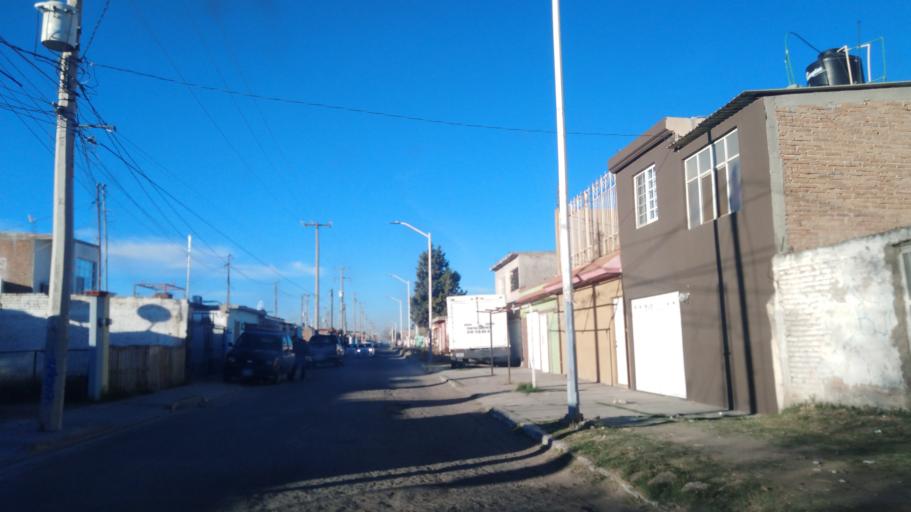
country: MX
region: Durango
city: Victoria de Durango
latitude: 24.0574
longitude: -104.6006
